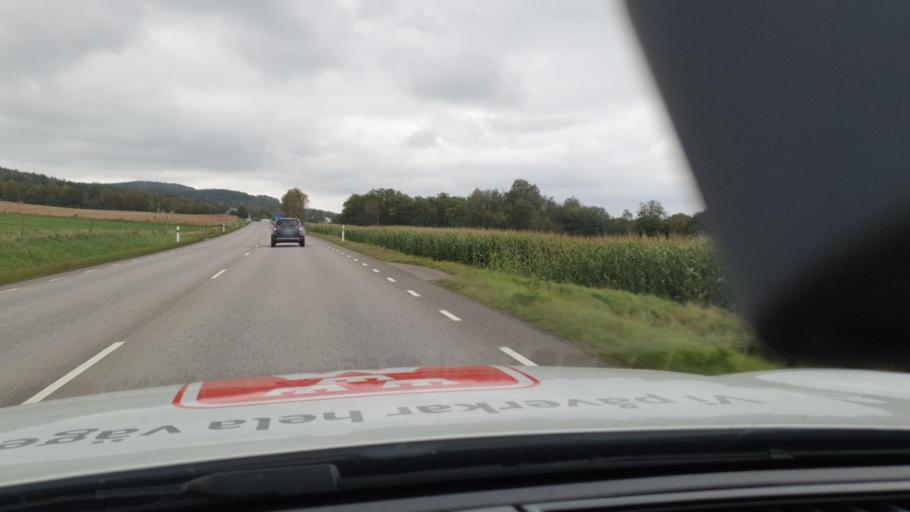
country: SE
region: Halland
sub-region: Falkenbergs Kommun
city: Falkenberg
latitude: 56.9756
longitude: 12.5768
